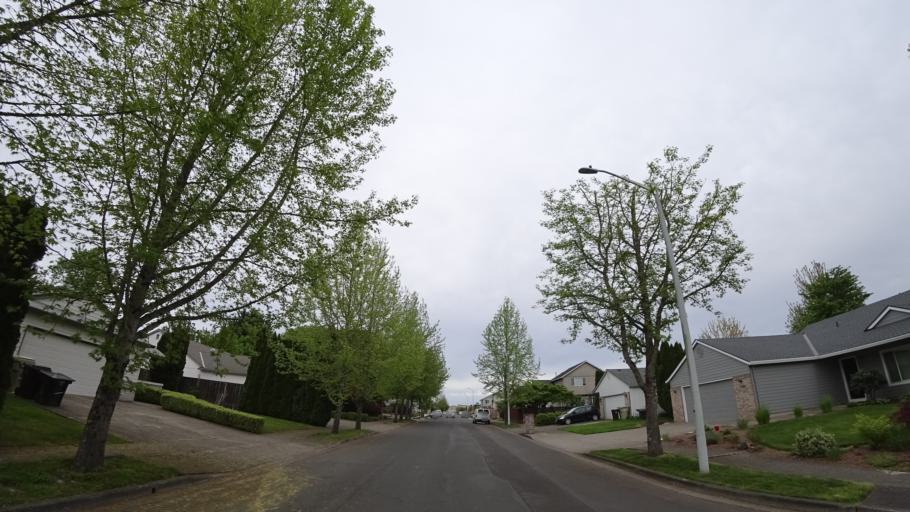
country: US
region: Oregon
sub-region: Washington County
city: Aloha
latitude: 45.5101
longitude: -122.9089
